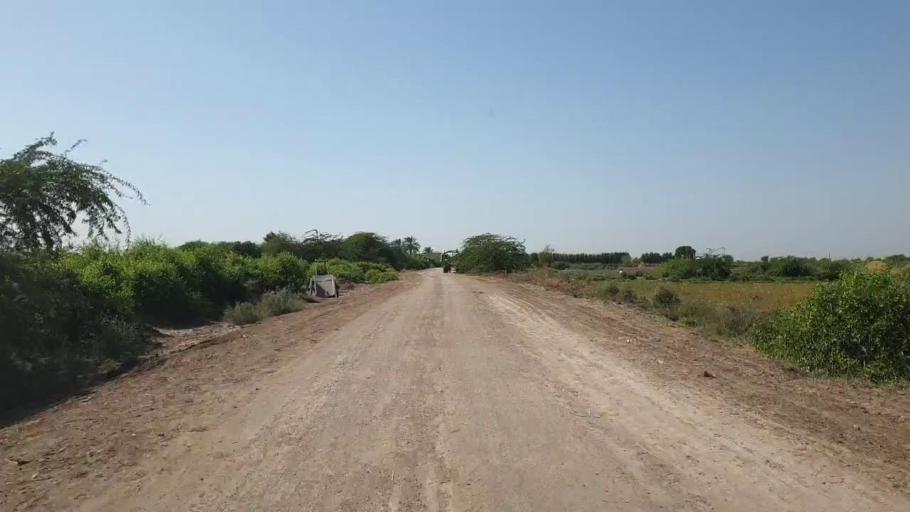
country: PK
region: Sindh
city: Tando Bago
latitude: 24.7049
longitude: 69.0286
